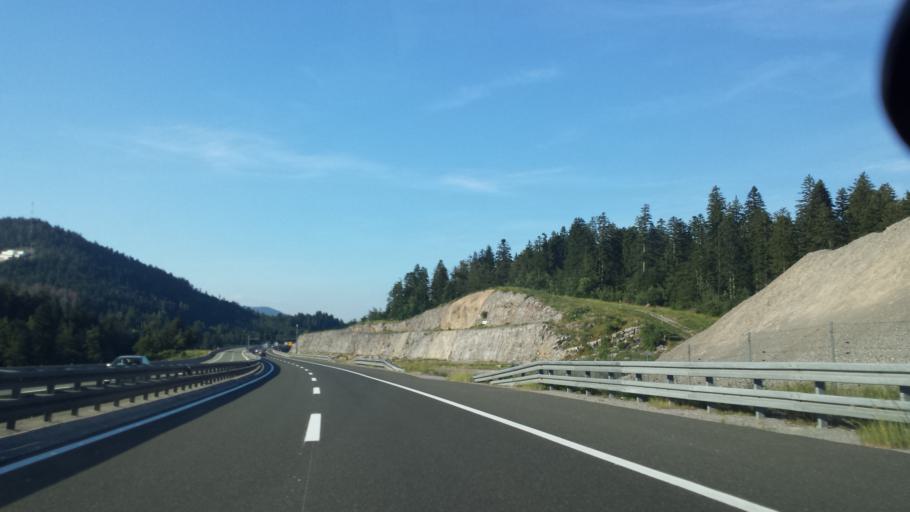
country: HR
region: Primorsko-Goranska
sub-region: Grad Delnice
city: Delnice
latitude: 45.3512
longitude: 14.7592
